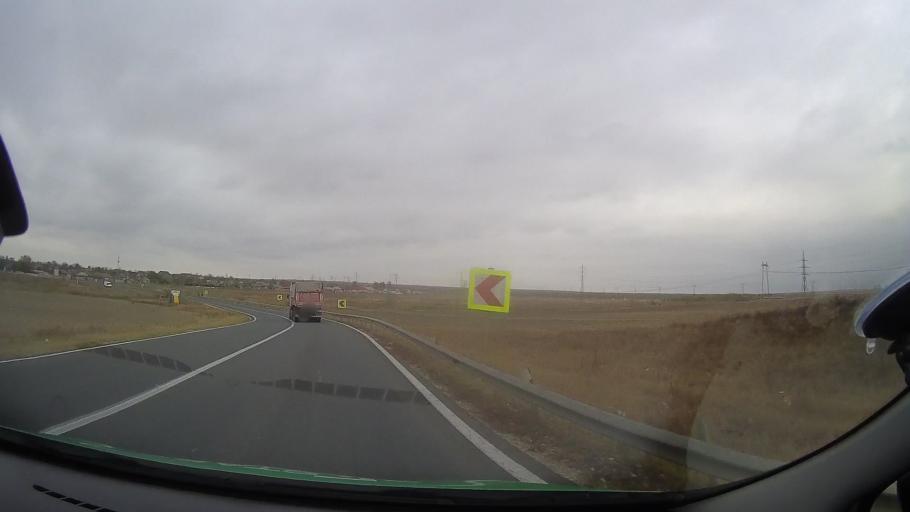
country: RO
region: Constanta
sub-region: Comuna Castelu
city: Castelu
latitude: 44.2585
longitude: 28.3482
